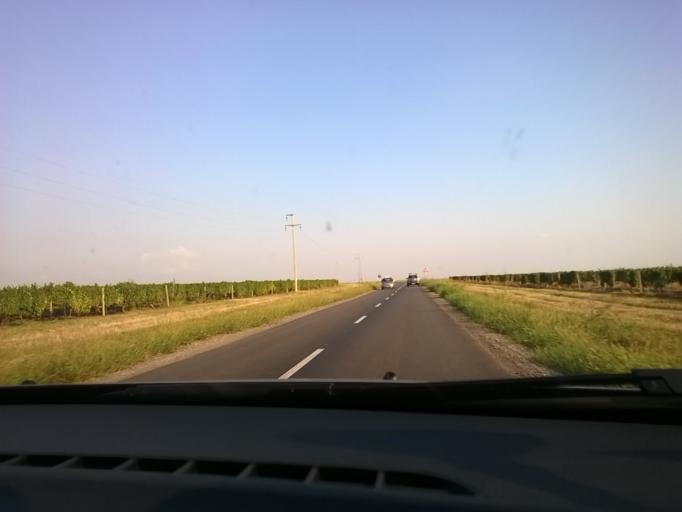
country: RS
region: Autonomna Pokrajina Vojvodina
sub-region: Juznobanatski Okrug
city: Vrsac
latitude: 45.1033
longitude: 21.3211
